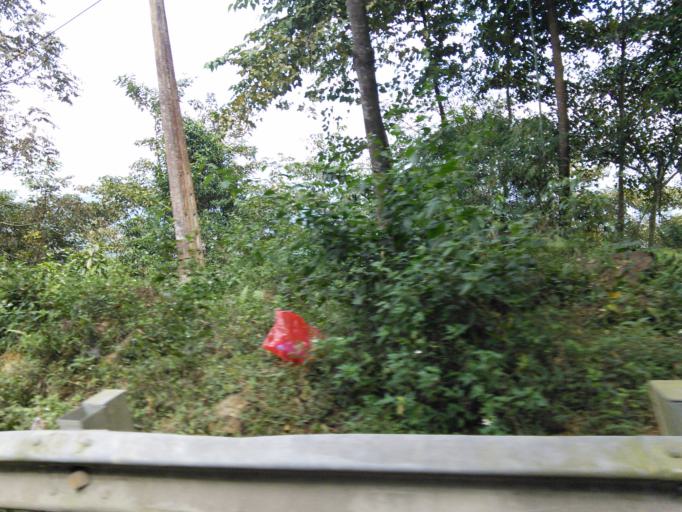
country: VN
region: Lao Cai
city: Lao Cai
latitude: 22.4478
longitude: 103.9344
